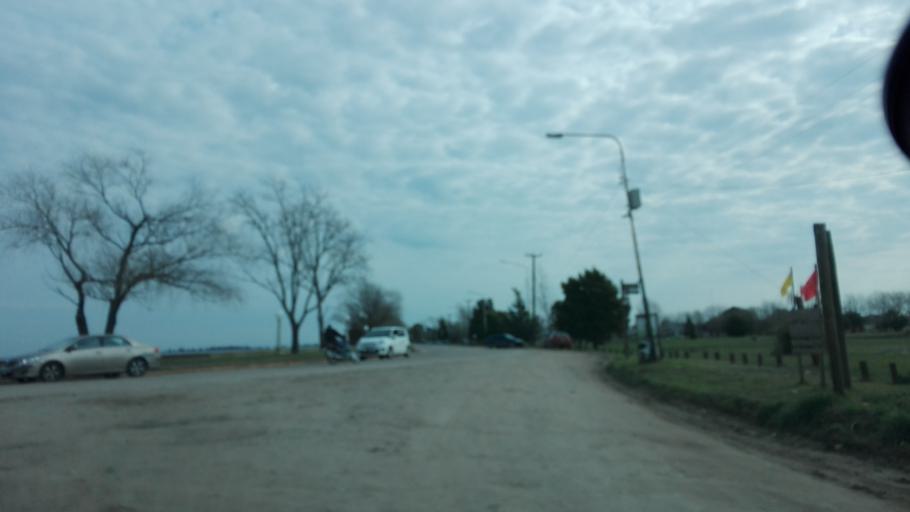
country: AR
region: Buenos Aires
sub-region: Partido de Chascomus
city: Chascomus
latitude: -35.5828
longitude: -57.9976
